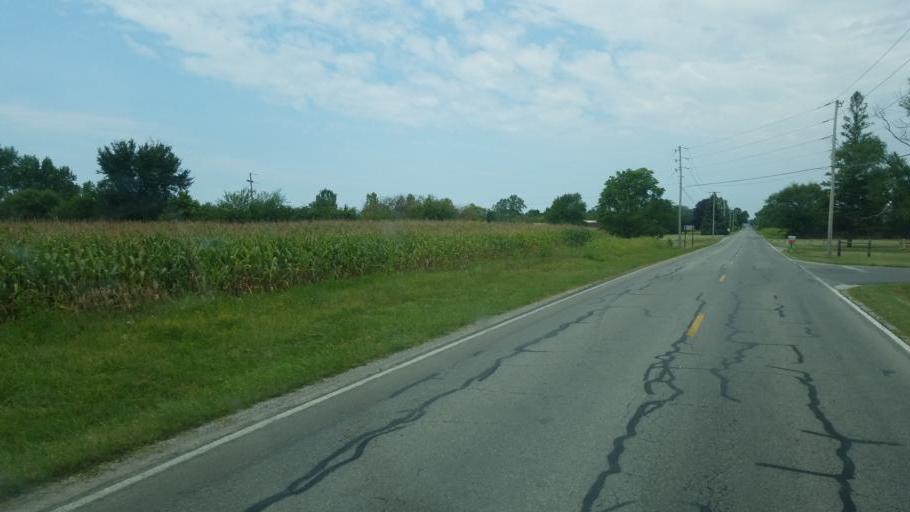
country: US
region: Ohio
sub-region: Marion County
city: Marion
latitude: 40.5648
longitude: -83.1646
